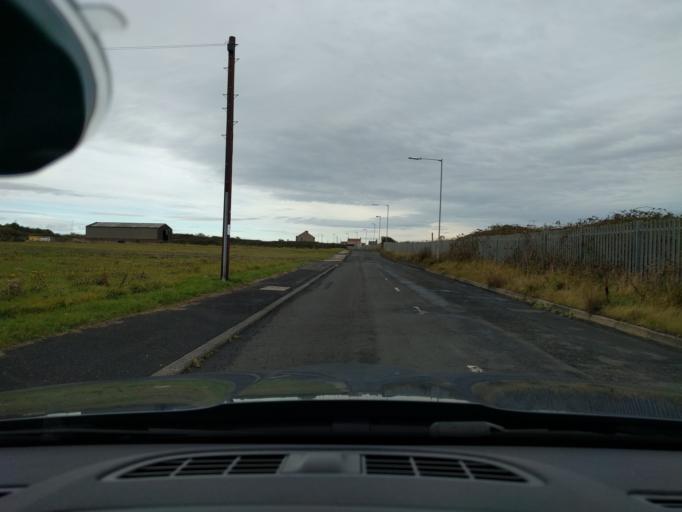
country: GB
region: England
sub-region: Northumberland
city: Blyth
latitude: 55.1479
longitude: -1.5222
